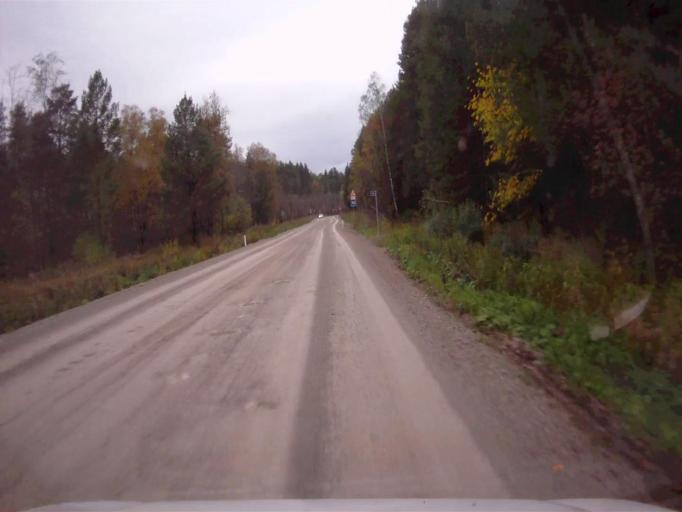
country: RU
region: Chelyabinsk
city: Nyazepetrovsk
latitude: 56.0444
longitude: 59.5052
